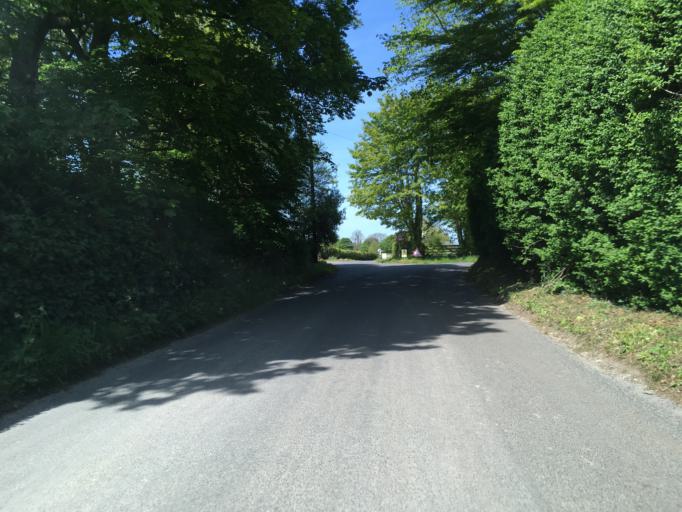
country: GB
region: England
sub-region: Gloucestershire
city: Cirencester
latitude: 51.6776
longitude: -1.9945
